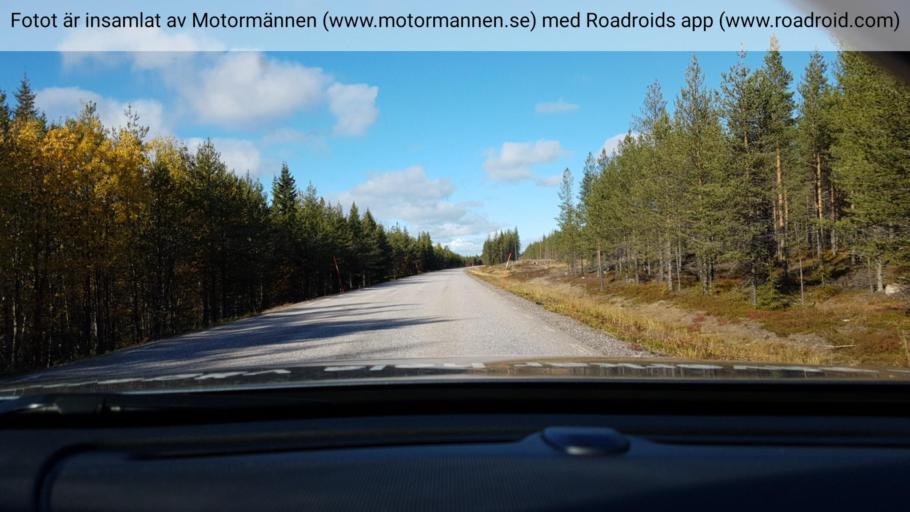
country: SE
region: Norrbotten
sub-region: Arvidsjaurs Kommun
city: Arvidsjaur
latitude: 65.7318
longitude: 18.6445
